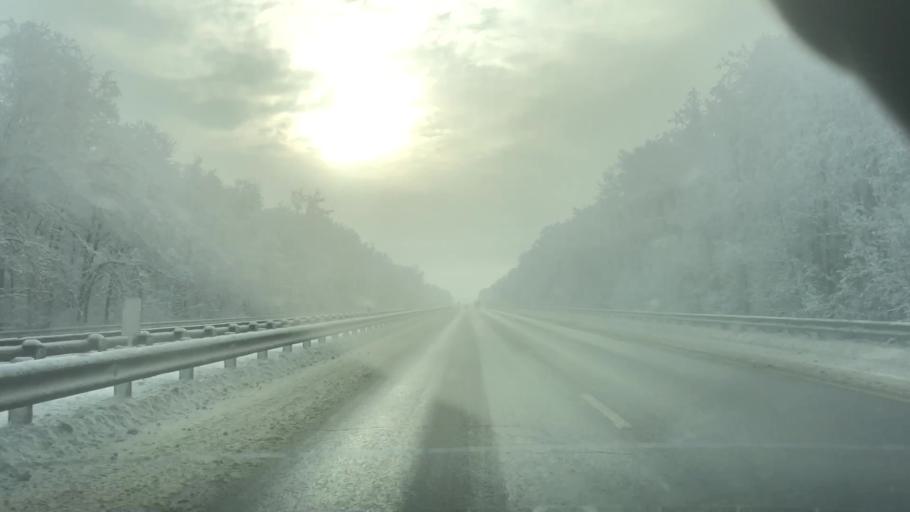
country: RU
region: Tula
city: Venev
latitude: 54.3680
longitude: 38.1547
